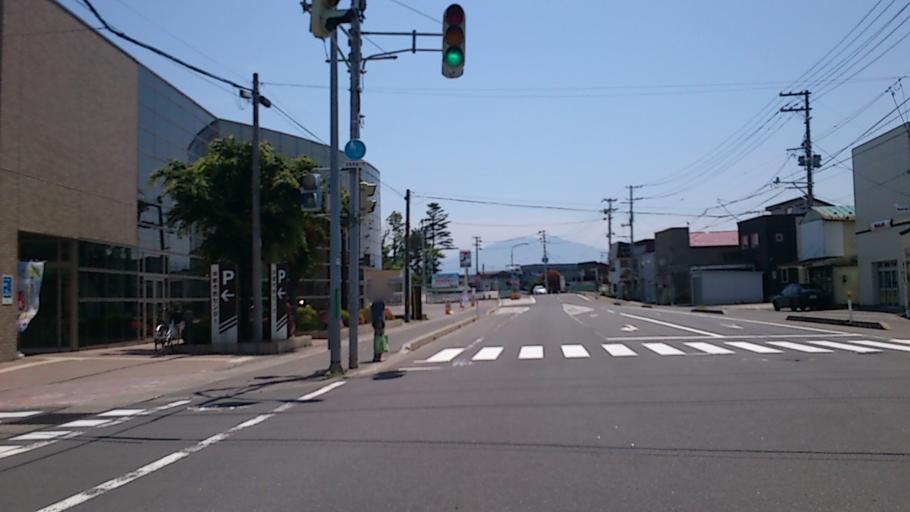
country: JP
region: Aomori
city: Aomori Shi
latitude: 40.8327
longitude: 140.7238
